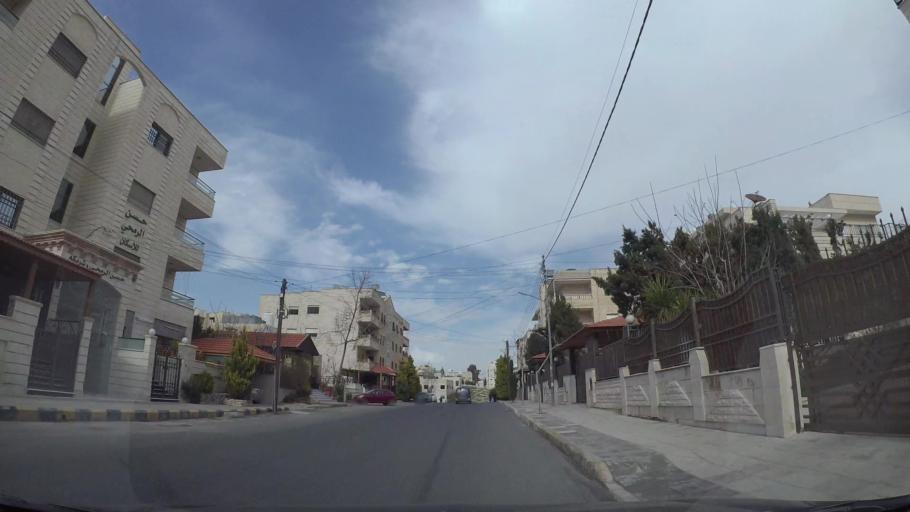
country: JO
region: Amman
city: Amman
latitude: 32.0051
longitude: 35.9361
